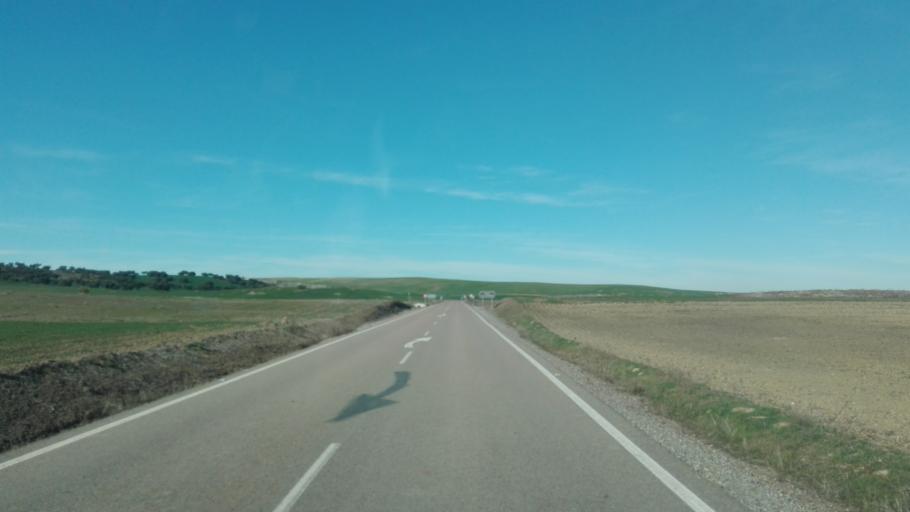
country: ES
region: Extremadura
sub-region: Provincia de Badajoz
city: Maguilla
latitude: 38.3385
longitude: -5.8978
